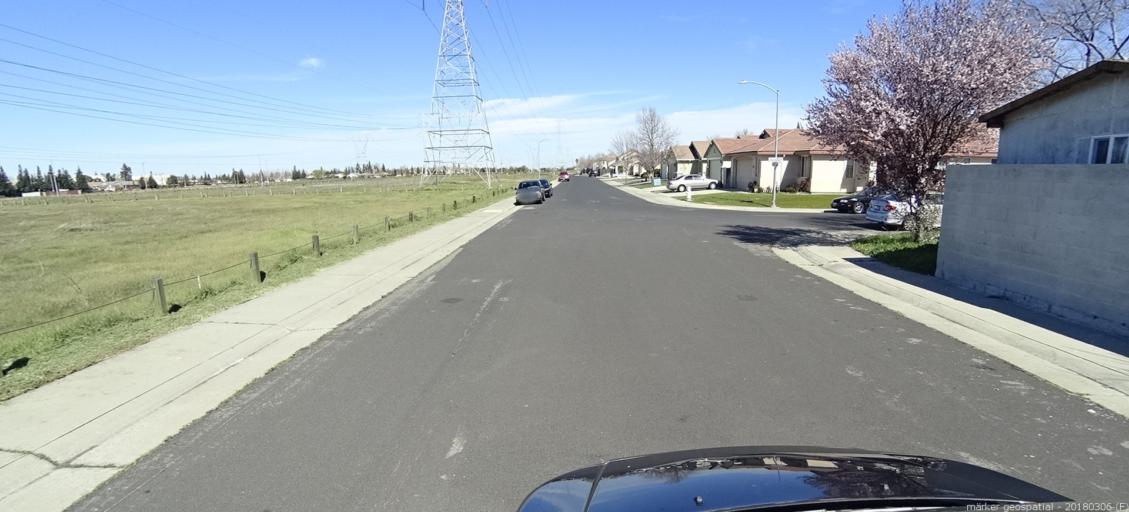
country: US
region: California
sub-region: Sacramento County
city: Vineyard
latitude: 38.4548
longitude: -121.3512
